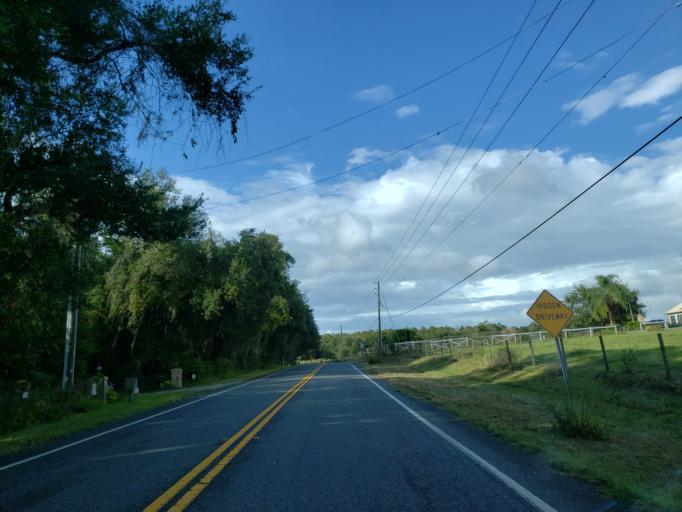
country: US
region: Florida
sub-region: Hernando County
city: Hill 'n Dale
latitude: 28.4671
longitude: -82.3006
